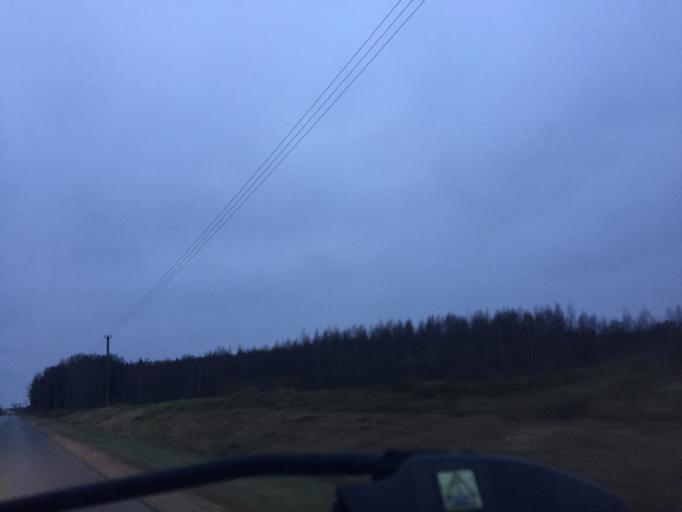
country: LV
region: Limbazu Rajons
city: Limbazi
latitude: 57.5967
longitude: 24.7960
